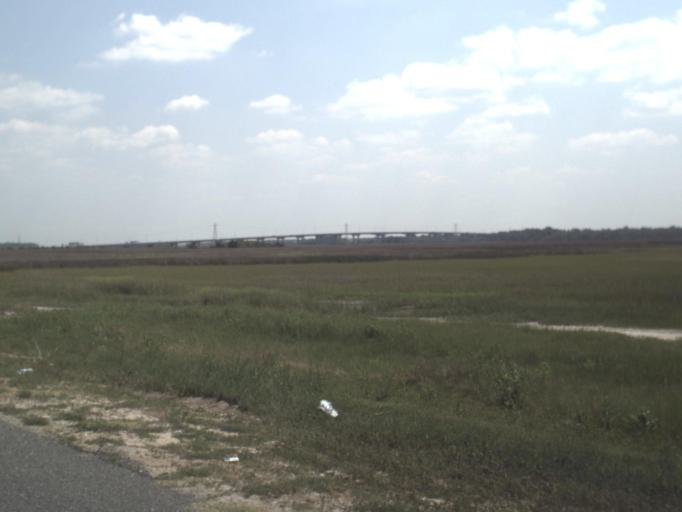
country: US
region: Florida
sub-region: Duval County
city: Atlantic Beach
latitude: 30.3777
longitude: -81.4371
